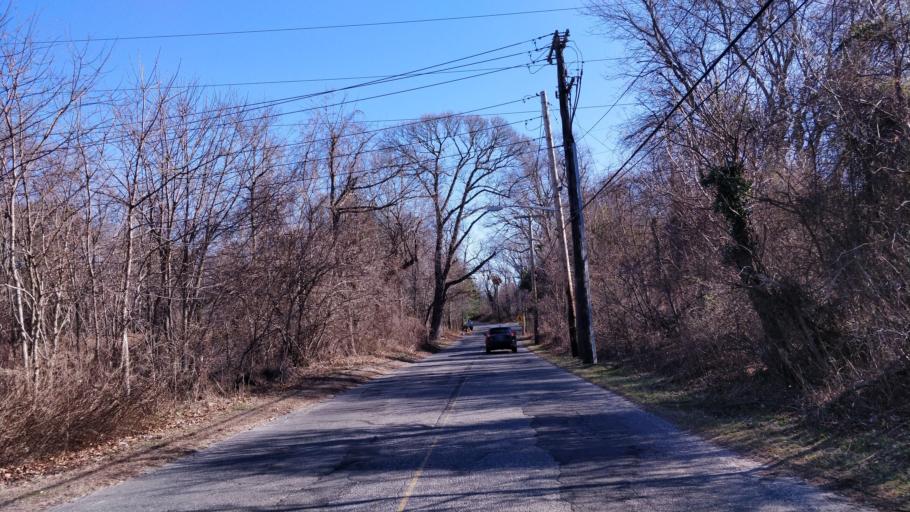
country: US
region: New York
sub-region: Suffolk County
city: Setauket-East Setauket
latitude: 40.9391
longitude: -73.0871
